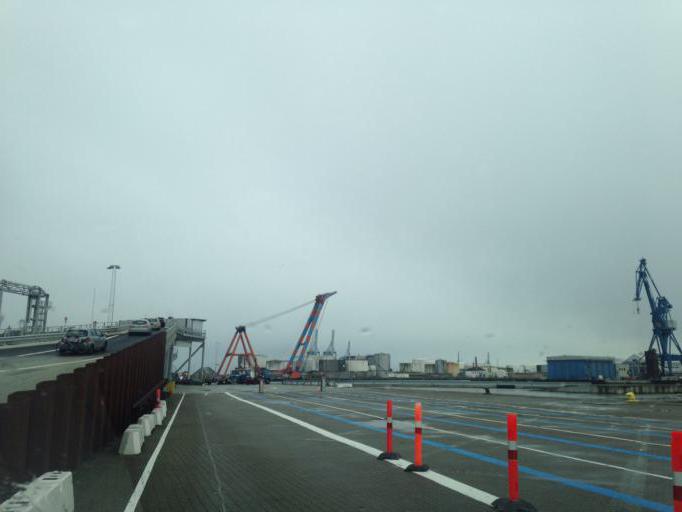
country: DK
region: Central Jutland
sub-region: Arhus Kommune
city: Arhus
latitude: 56.1604
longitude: 10.2204
